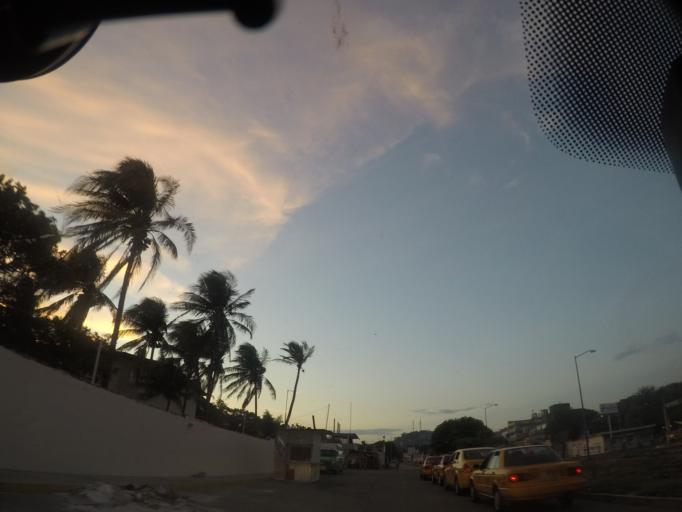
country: MX
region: Oaxaca
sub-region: Salina Cruz
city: Salina Cruz
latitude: 16.1781
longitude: -95.1954
